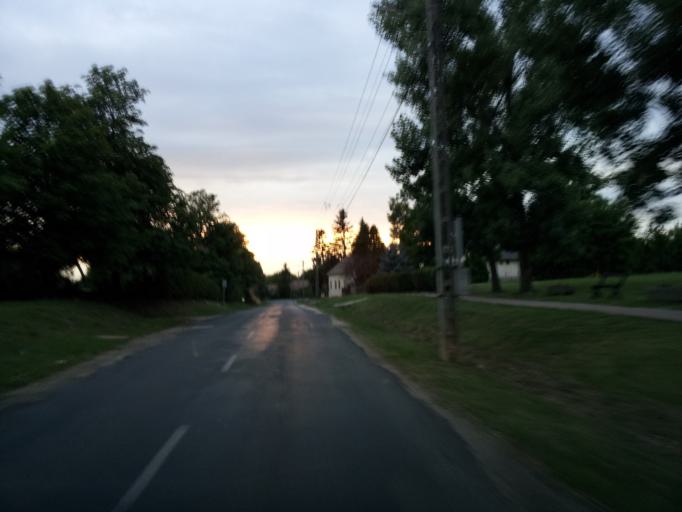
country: HU
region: Somogy
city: Adand
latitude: 46.8570
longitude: 18.1560
